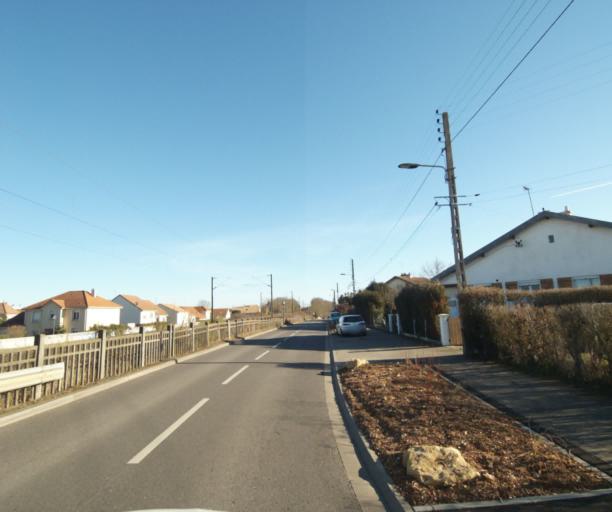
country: FR
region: Lorraine
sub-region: Departement de Meurthe-et-Moselle
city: Laneuveville-devant-Nancy
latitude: 48.6599
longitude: 6.2220
